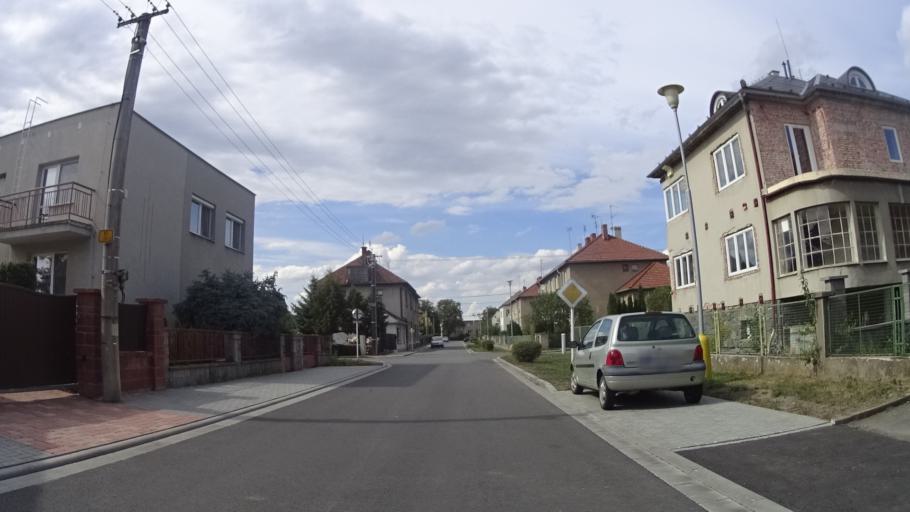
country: CZ
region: Olomoucky
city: Litovel
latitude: 49.6999
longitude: 17.0864
